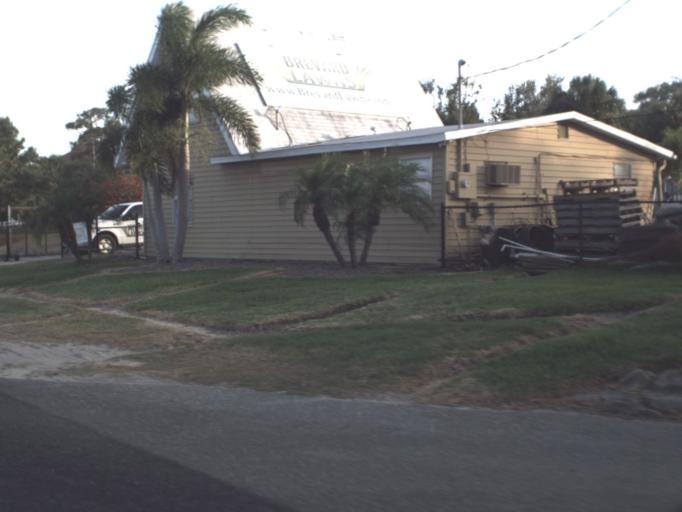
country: US
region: Florida
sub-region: Brevard County
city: South Patrick Shores
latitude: 28.2345
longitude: -80.6752
